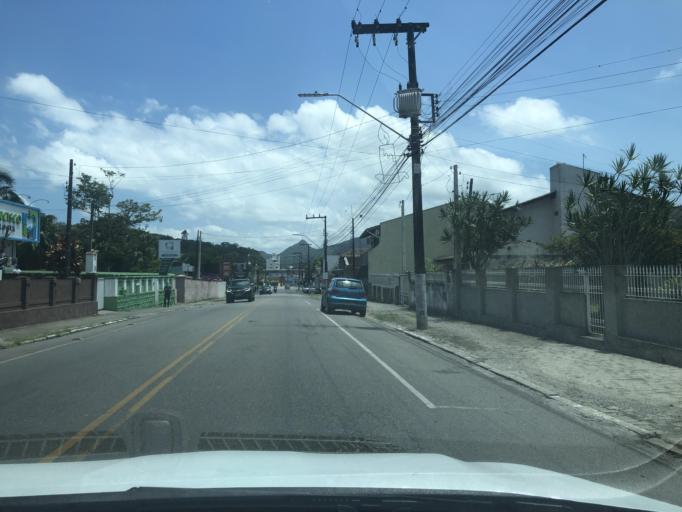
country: BR
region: Santa Catarina
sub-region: Sao Francisco Do Sul
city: Sao Francisco do Sul
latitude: -26.2529
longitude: -48.6423
